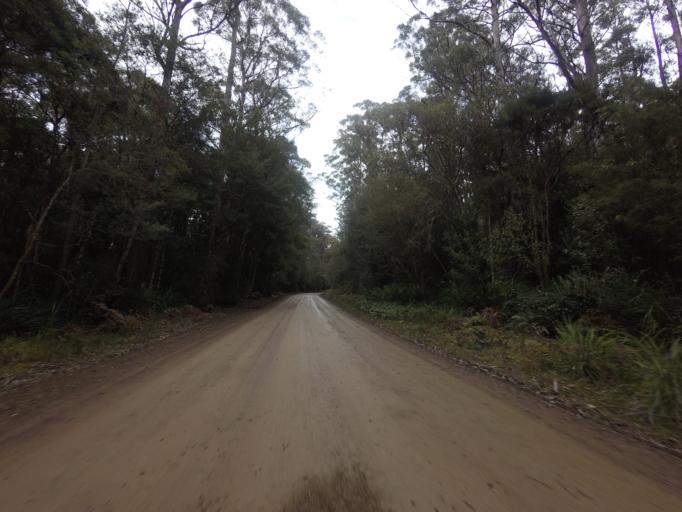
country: AU
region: Tasmania
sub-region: Huon Valley
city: Geeveston
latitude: -43.4153
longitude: 146.8899
